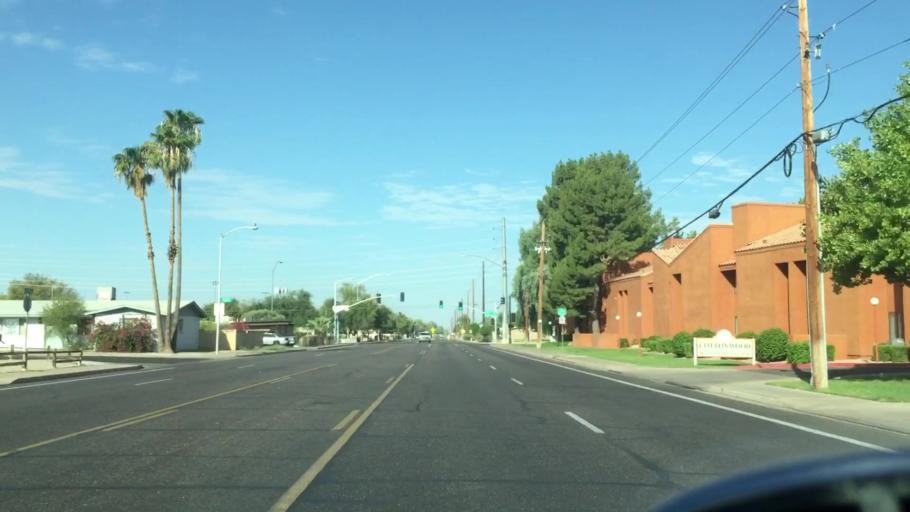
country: US
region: Arizona
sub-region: Maricopa County
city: Mesa
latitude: 33.4005
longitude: -111.8470
